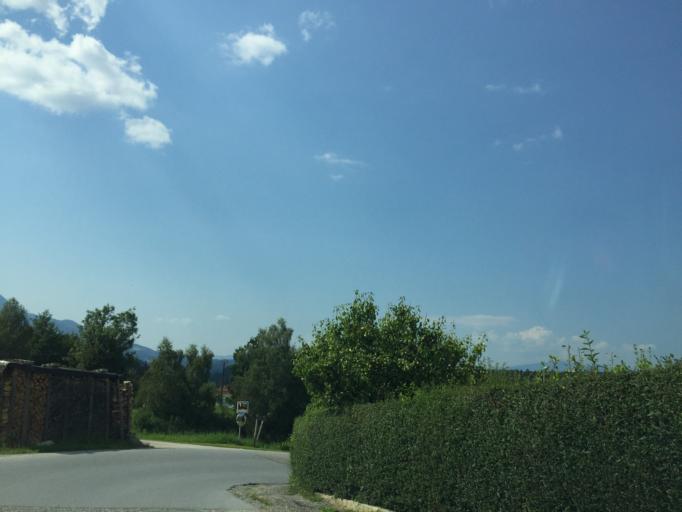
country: SI
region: Slovenj Gradec
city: Smartno pri Slovenj Gradcu
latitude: 46.4511
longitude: 15.1199
